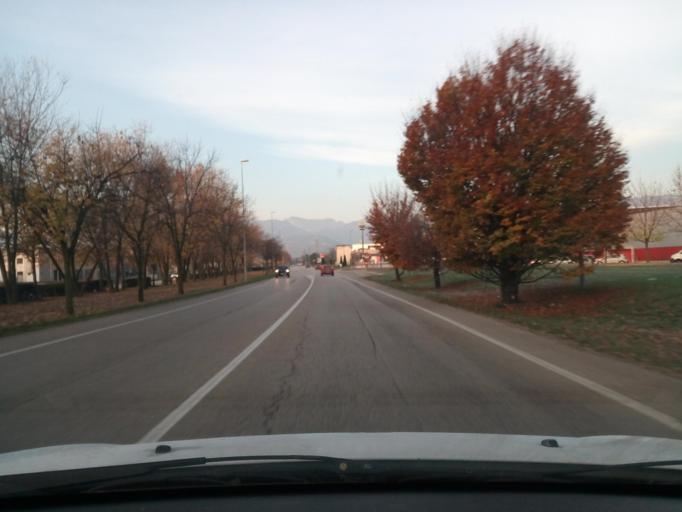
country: IT
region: Veneto
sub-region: Provincia di Vicenza
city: Santorso
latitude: 45.7204
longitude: 11.4018
